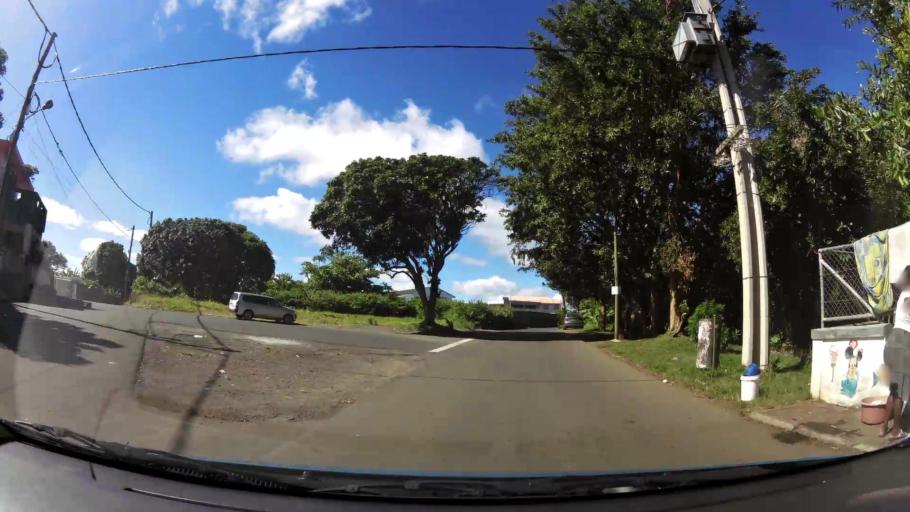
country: MU
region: Plaines Wilhems
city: Vacoas
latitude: -20.3335
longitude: 57.4759
